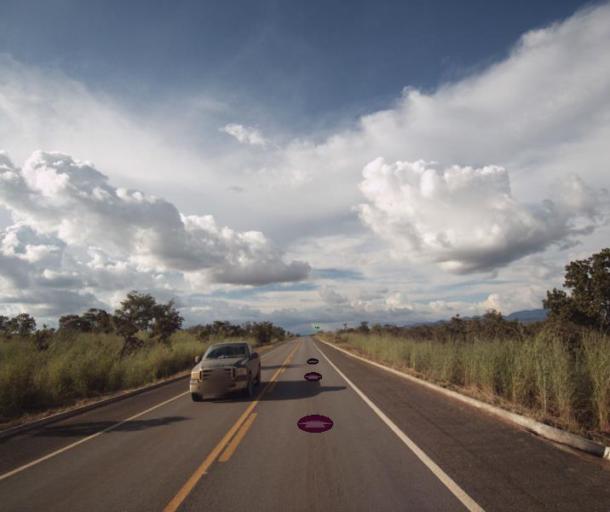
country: BR
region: Goias
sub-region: Barro Alto
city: Barro Alto
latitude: -14.8214
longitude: -48.6380
